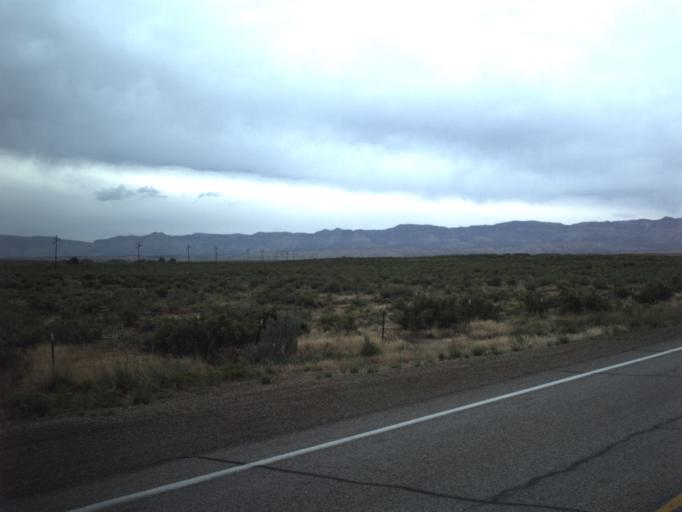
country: US
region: Utah
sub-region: Carbon County
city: East Carbon City
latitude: 39.5268
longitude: -110.5722
